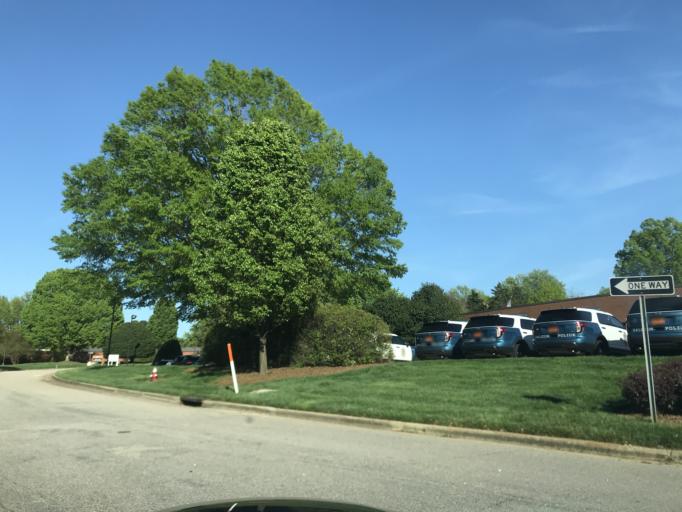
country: US
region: North Carolina
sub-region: Wake County
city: Raleigh
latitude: 35.8585
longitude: -78.5787
